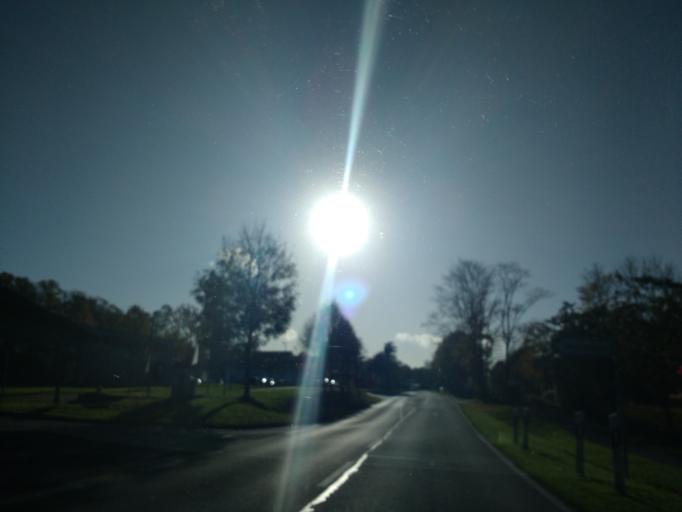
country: DE
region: Mecklenburg-Vorpommern
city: Klutz
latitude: 53.9694
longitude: 11.1725
